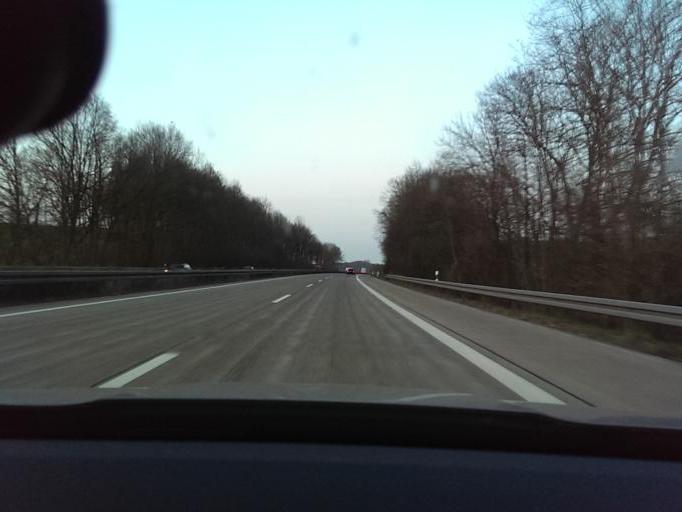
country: DE
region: Lower Saxony
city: Kalefeld
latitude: 51.8055
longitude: 10.0917
